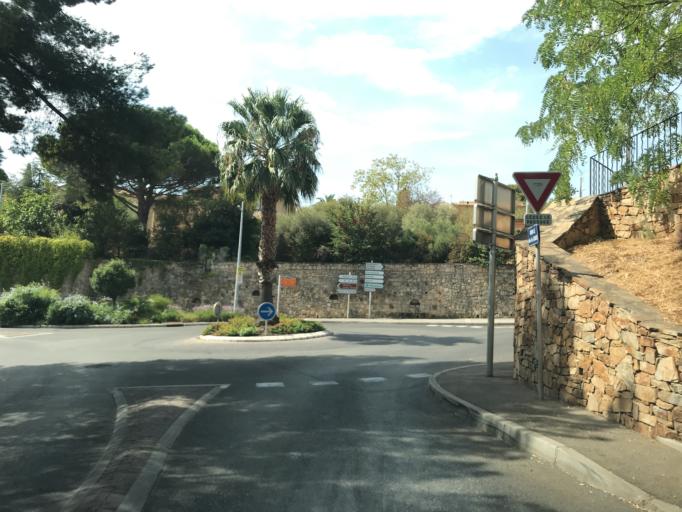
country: FR
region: Provence-Alpes-Cote d'Azur
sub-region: Departement du Var
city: Bandol
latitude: 43.1392
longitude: 5.7509
